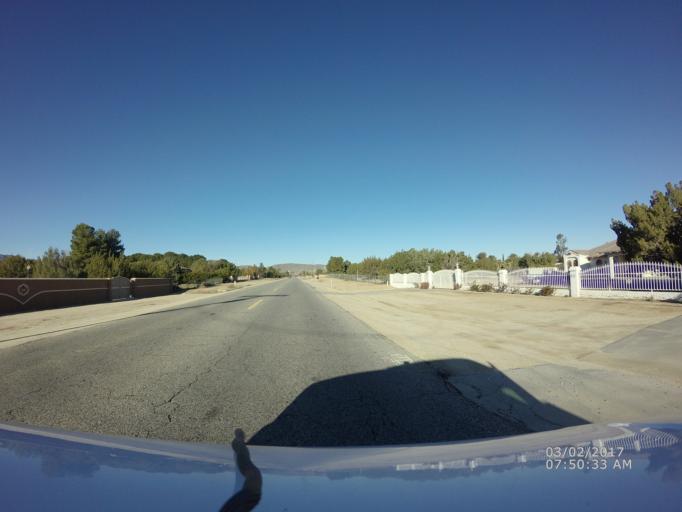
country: US
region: California
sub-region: Los Angeles County
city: Desert View Highlands
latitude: 34.6164
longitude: -118.1685
